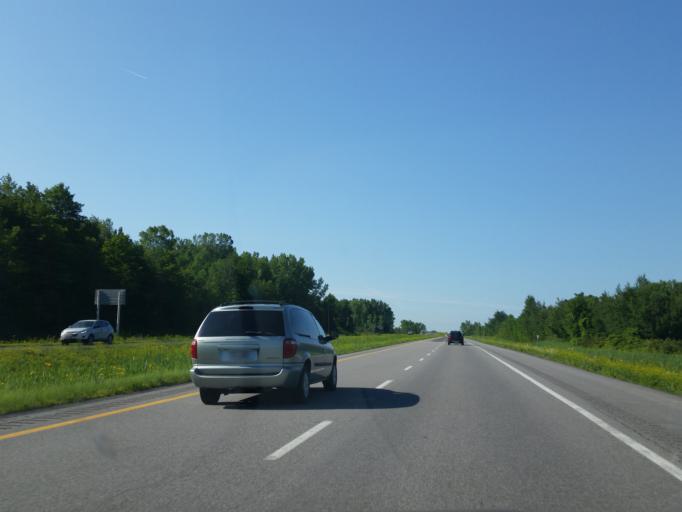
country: CA
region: Quebec
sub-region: Monteregie
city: Napierville
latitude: 45.2470
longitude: -73.4726
